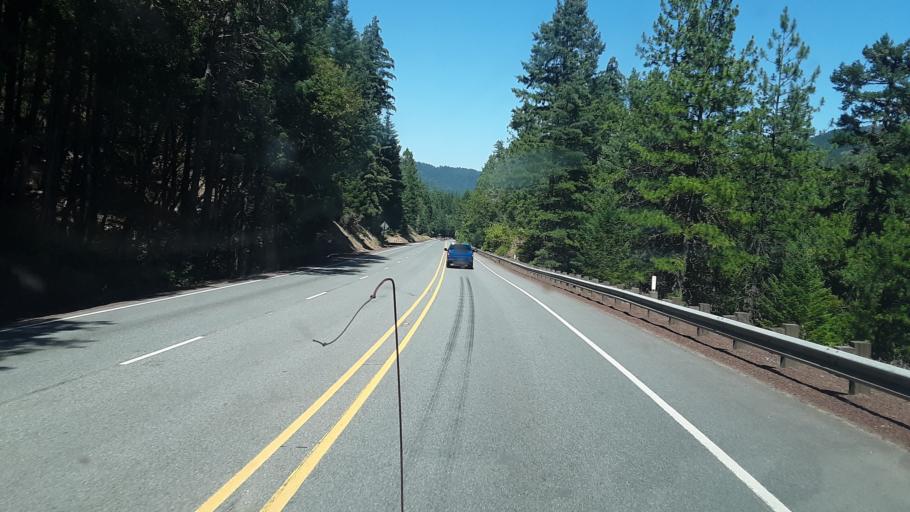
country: US
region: Oregon
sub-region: Josephine County
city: Cave Junction
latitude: 42.3387
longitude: -123.5779
